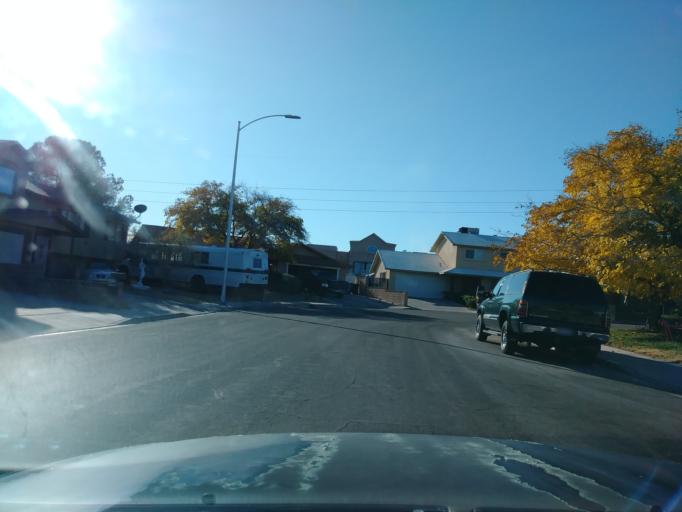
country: US
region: Nevada
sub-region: Clark County
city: Spring Valley
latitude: 36.1600
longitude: -115.2534
